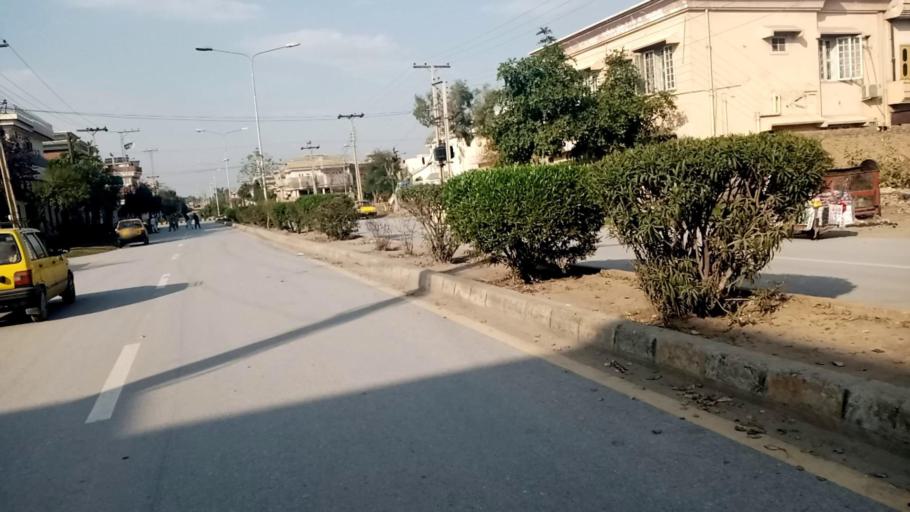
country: PK
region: Khyber Pakhtunkhwa
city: Peshawar
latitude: 33.9880
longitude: 71.4456
